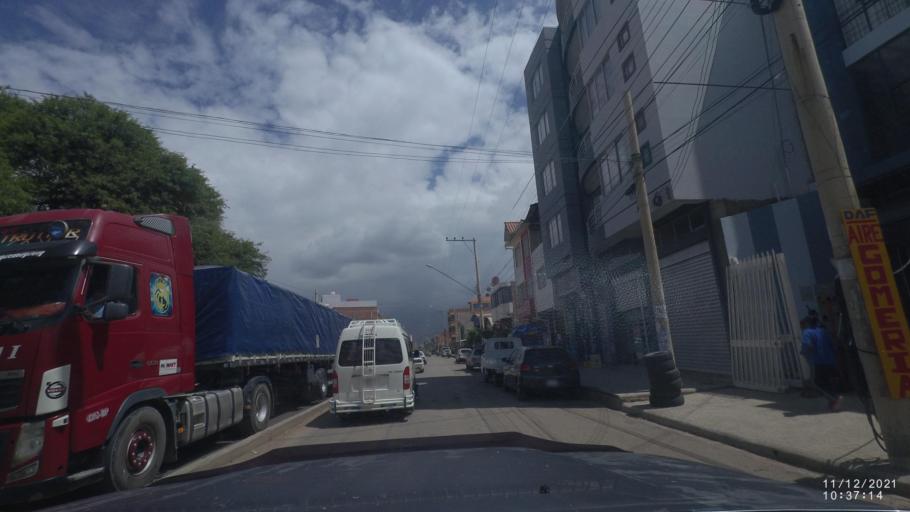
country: BO
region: Cochabamba
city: Cochabamba
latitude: -17.4464
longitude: -66.1252
